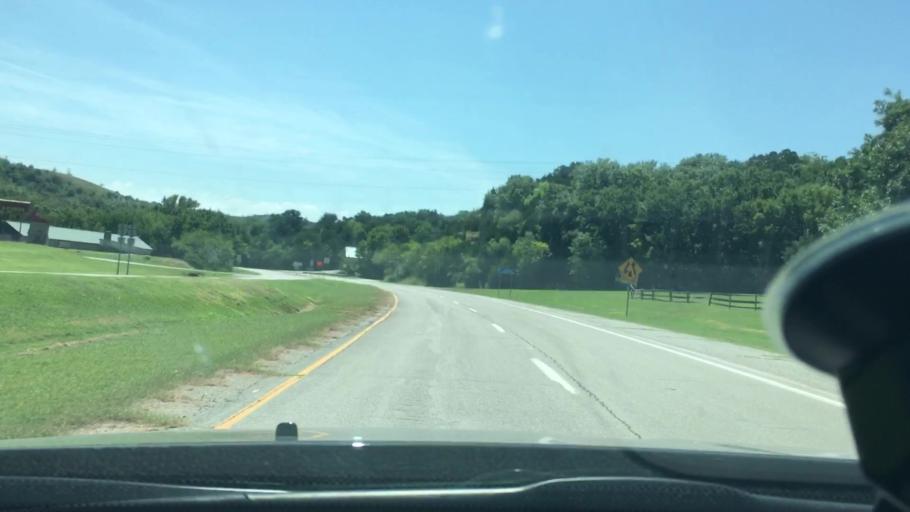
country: US
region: Oklahoma
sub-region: Murray County
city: Davis
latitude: 34.4476
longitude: -97.1356
